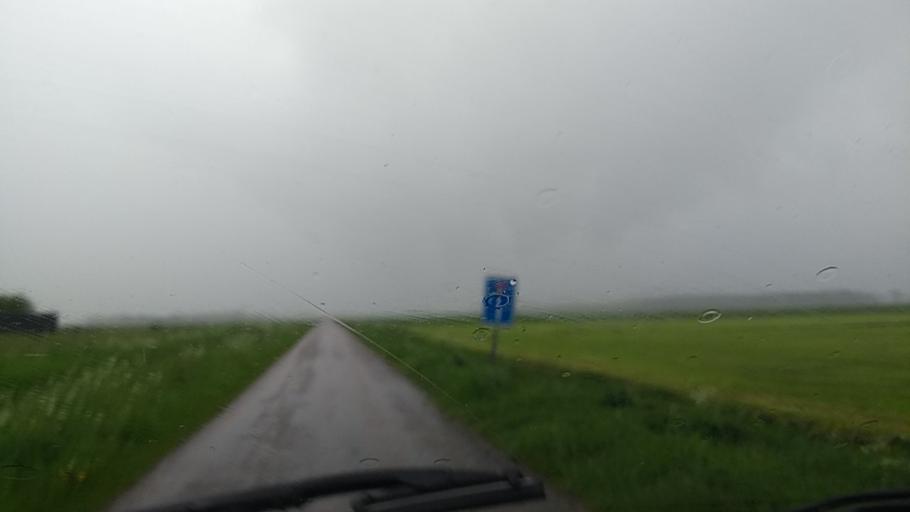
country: NL
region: Drenthe
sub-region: Gemeente Westerveld
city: Havelte
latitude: 52.7680
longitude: 6.2910
